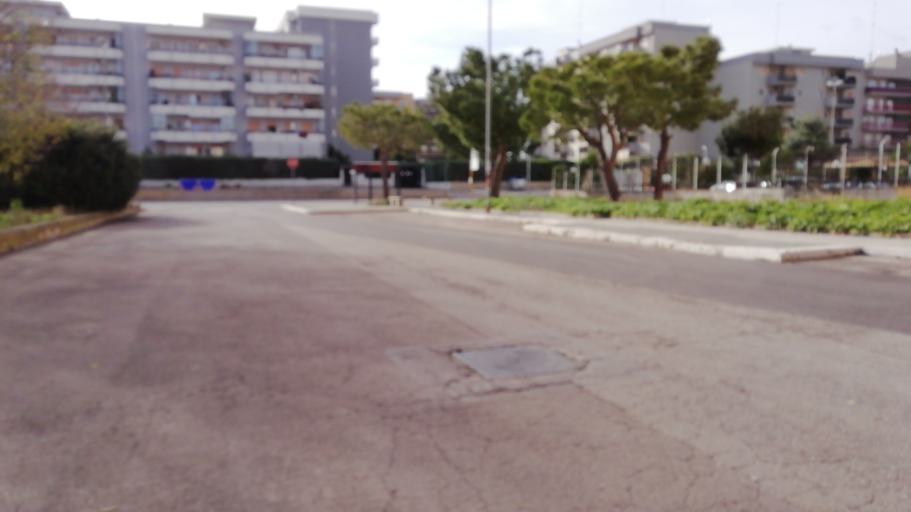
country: IT
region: Apulia
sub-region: Provincia di Bari
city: Triggiano
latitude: 41.1008
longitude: 16.9017
